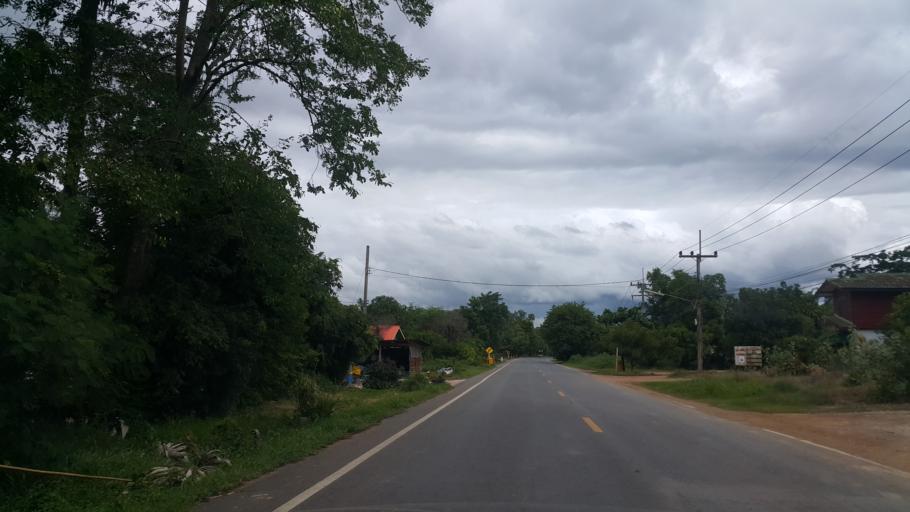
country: TH
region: Sukhothai
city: Ban Na
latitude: 17.0399
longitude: 99.7039
